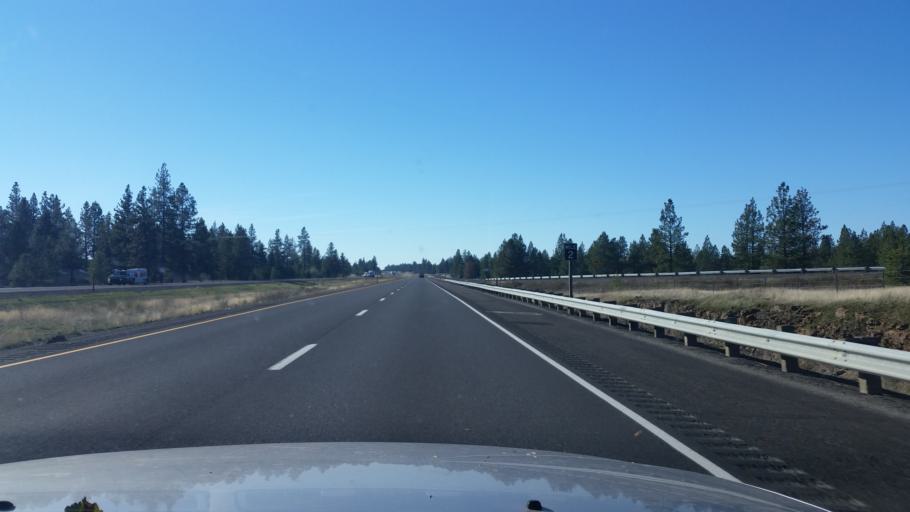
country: US
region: Washington
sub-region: Spokane County
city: Medical Lake
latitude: 47.4453
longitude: -117.7779
